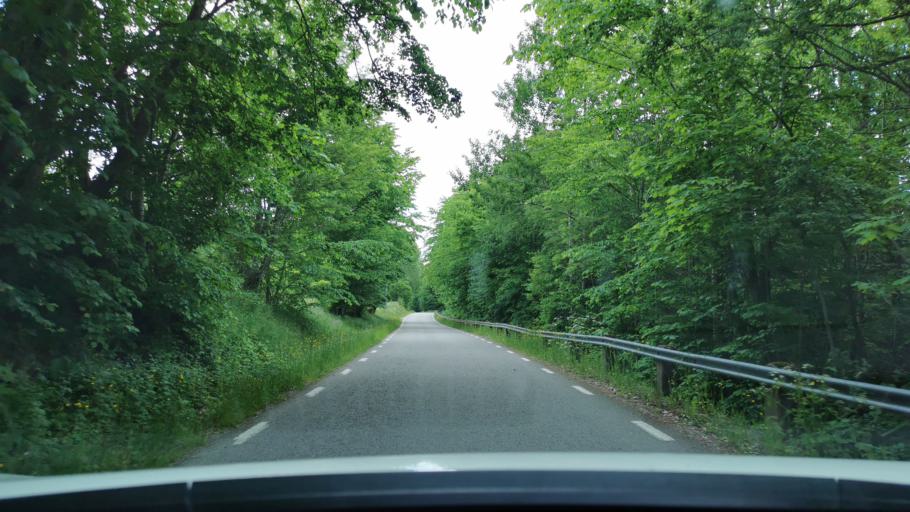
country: SE
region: Vaestra Goetaland
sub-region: Bengtsfors Kommun
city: Dals Langed
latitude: 58.8409
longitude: 12.3328
